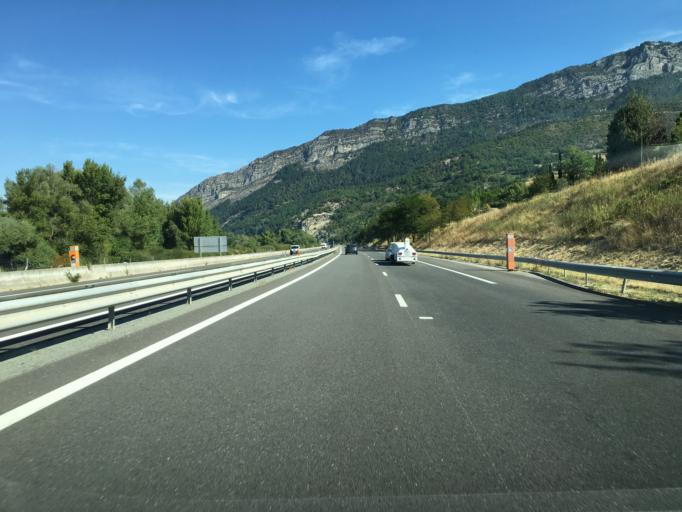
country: FR
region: Provence-Alpes-Cote d'Azur
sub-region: Departement des Alpes-de-Haute-Provence
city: Sisteron
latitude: 44.1807
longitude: 5.9553
